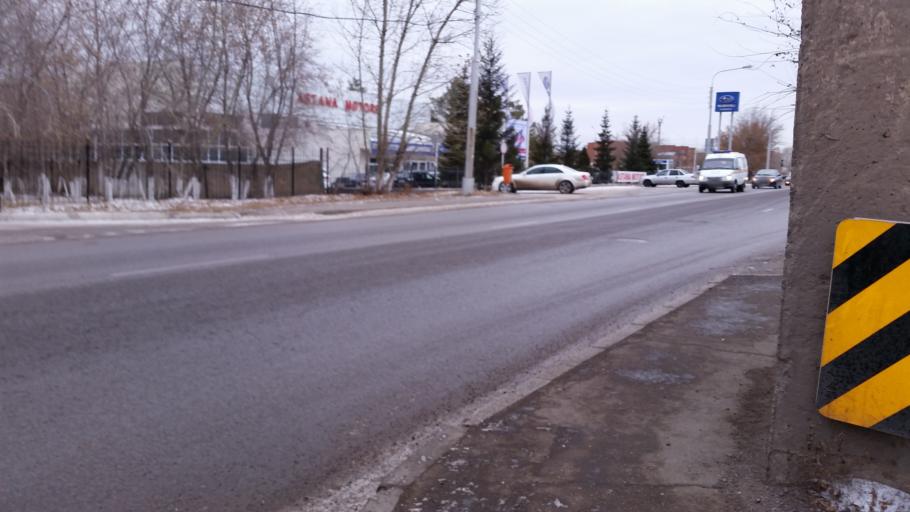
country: KZ
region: Astana Qalasy
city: Astana
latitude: 51.1613
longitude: 71.4823
